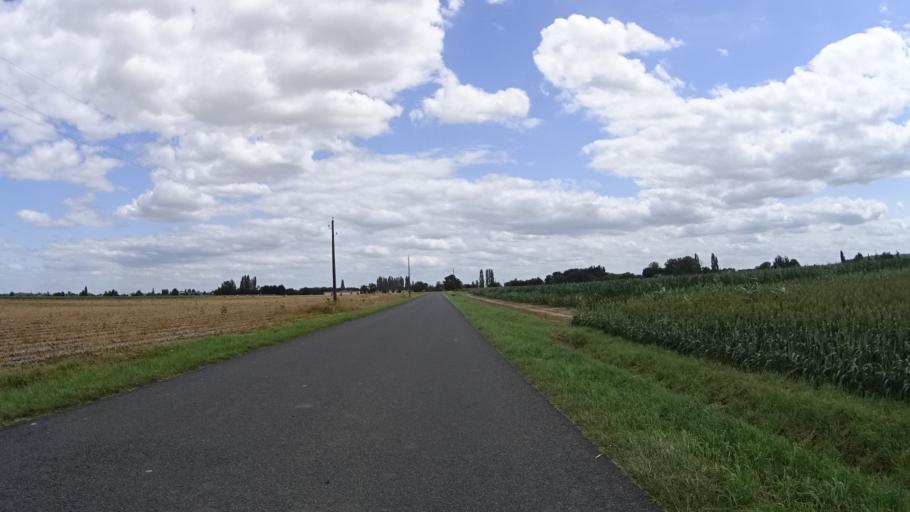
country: FR
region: Pays de la Loire
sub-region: Departement de Maine-et-Loire
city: Saint-Mathurin-sur-Loire
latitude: 47.4125
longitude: -0.3059
